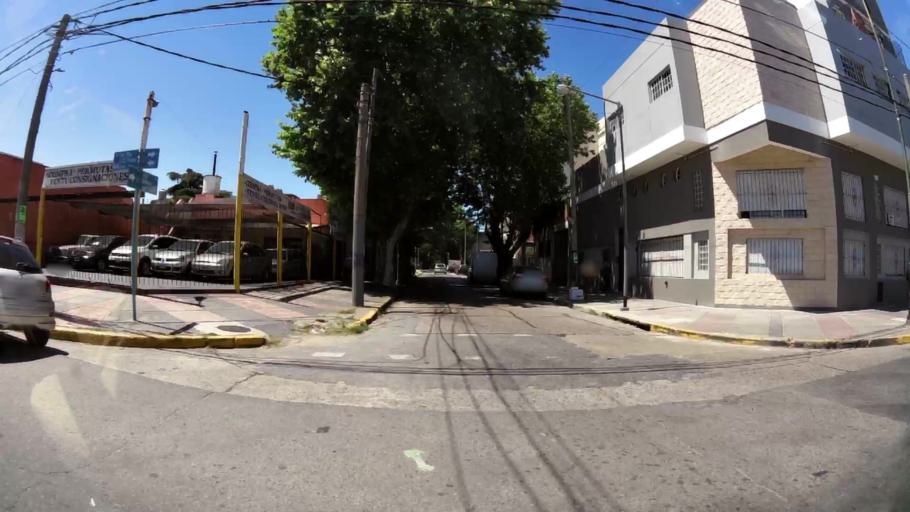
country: AR
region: Buenos Aires
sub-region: Partido de General San Martin
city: General San Martin
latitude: -34.5747
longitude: -58.5462
